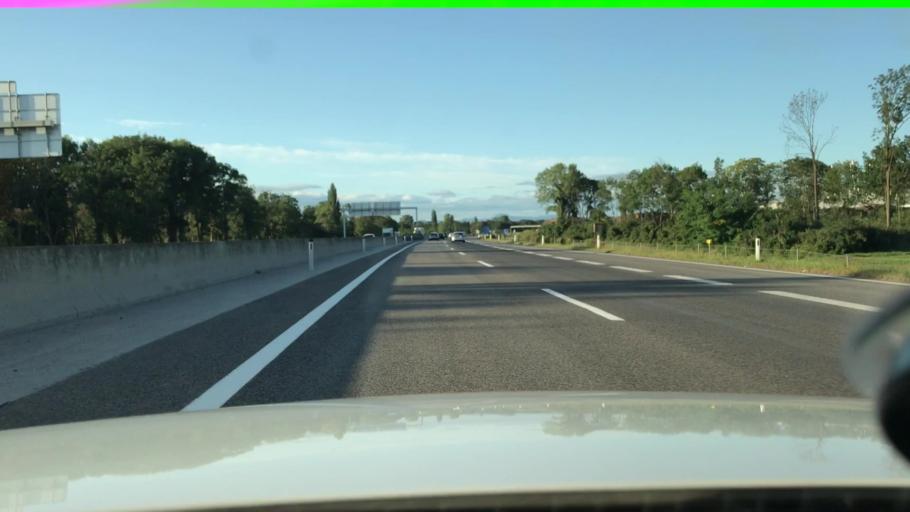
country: AT
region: Lower Austria
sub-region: Politischer Bezirk Sankt Polten
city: Herzogenburg
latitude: 48.2595
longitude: 15.6964
